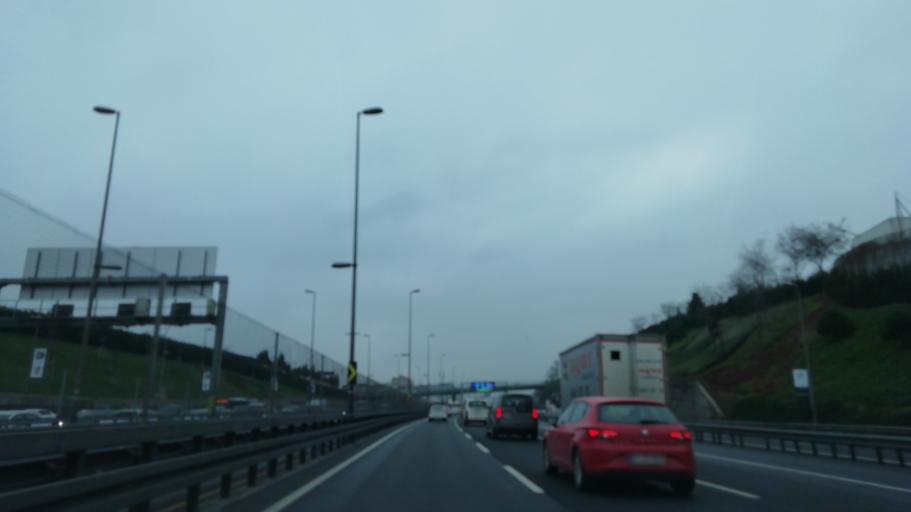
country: TR
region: Istanbul
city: Istanbul
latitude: 41.0509
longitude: 28.9493
